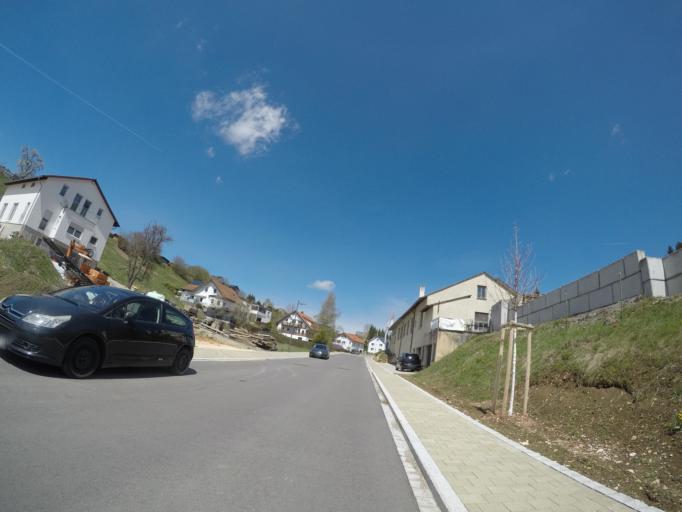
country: DE
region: Baden-Wuerttemberg
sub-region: Tuebingen Region
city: Westerheim
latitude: 48.5118
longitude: 9.6204
